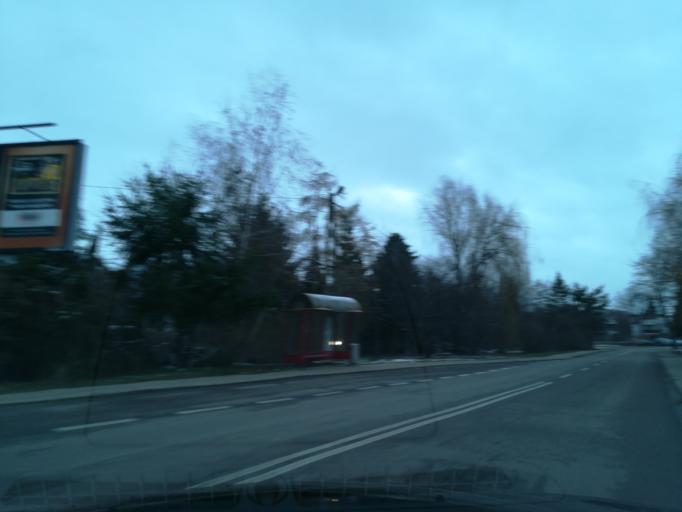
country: PL
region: Subcarpathian Voivodeship
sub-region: Rzeszow
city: Rzeszow
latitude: 50.0361
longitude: 22.0225
